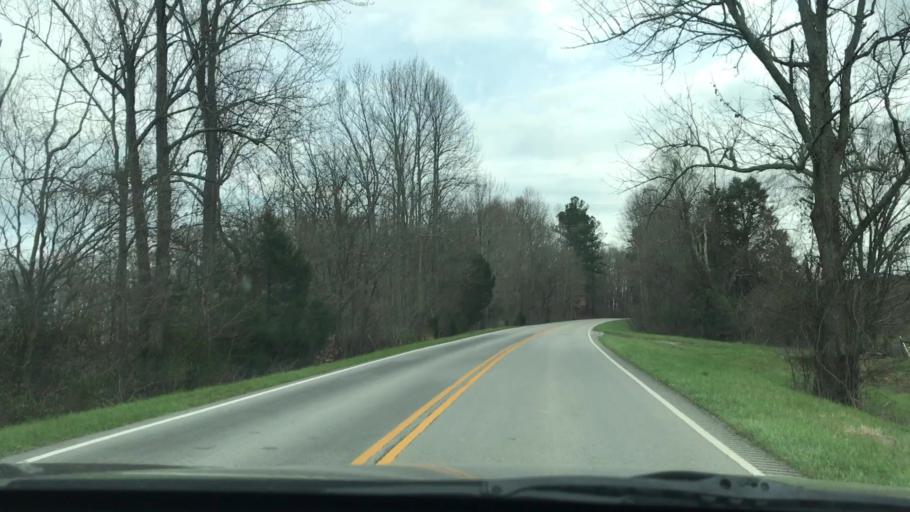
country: US
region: Kentucky
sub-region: Hart County
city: Munfordville
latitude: 37.3131
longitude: -85.7620
